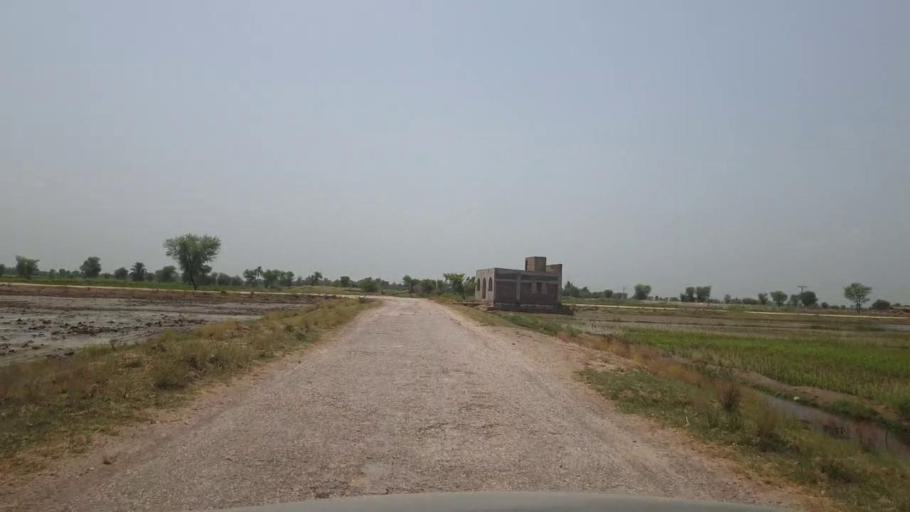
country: PK
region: Sindh
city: Garhi Yasin
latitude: 27.9120
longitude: 68.4040
